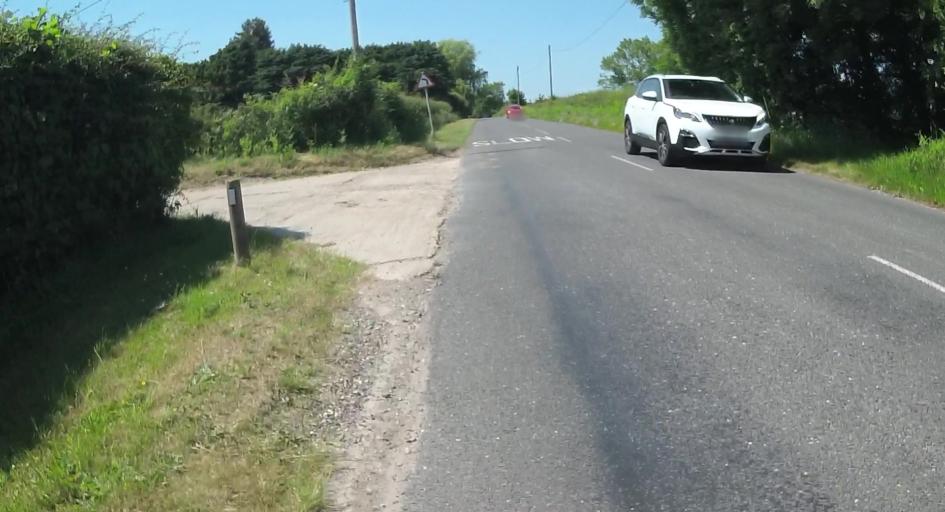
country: GB
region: England
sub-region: Hampshire
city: Kingsclere
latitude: 51.3620
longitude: -1.2289
